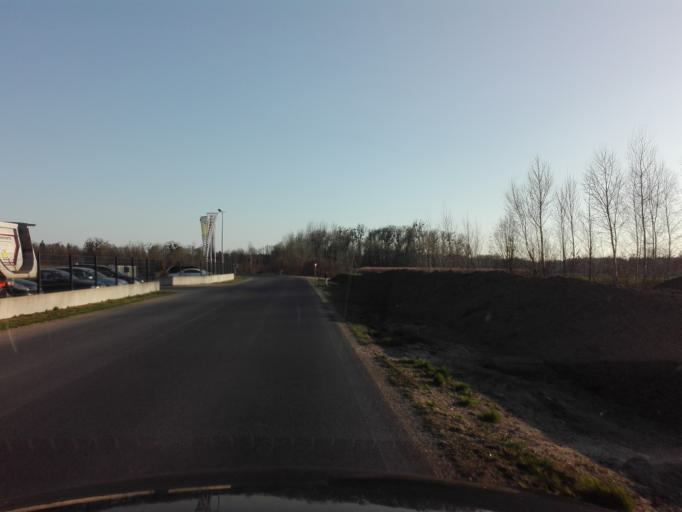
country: AT
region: Upper Austria
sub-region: Politischer Bezirk Perg
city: Perg
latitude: 48.2230
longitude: 14.6977
